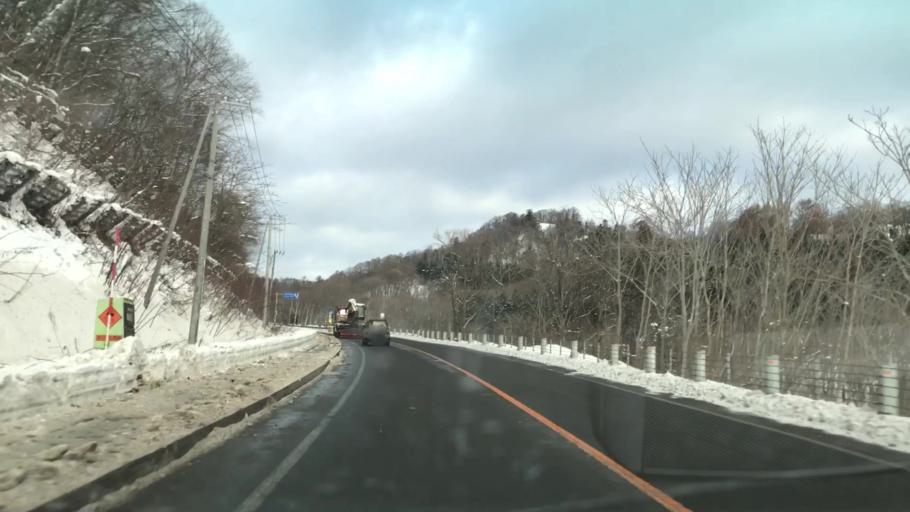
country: JP
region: Hokkaido
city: Yoichi
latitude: 43.2129
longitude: 140.7487
